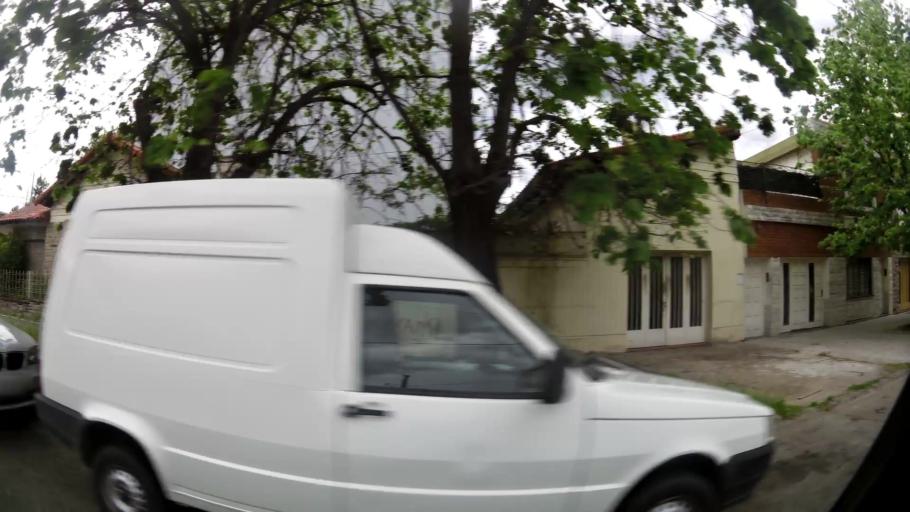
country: AR
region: Buenos Aires
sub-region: Partido de Lanus
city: Lanus
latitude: -34.6941
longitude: -58.3937
